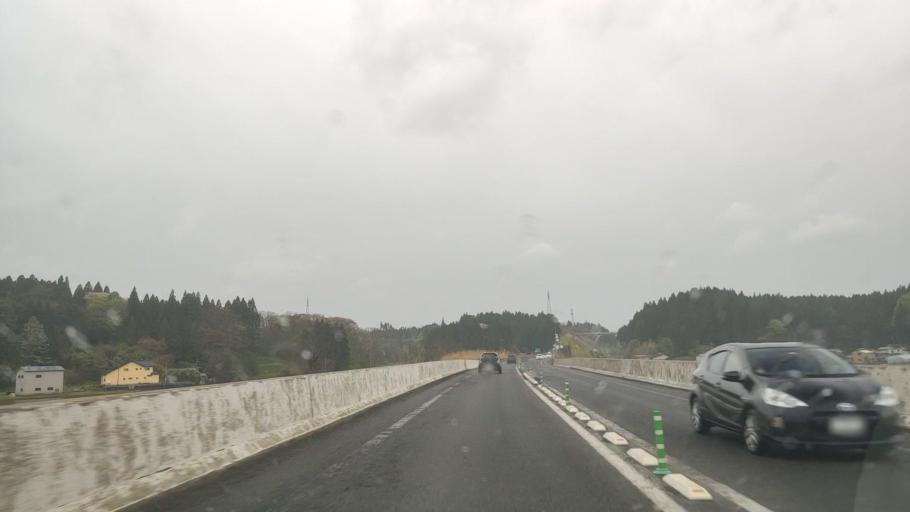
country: JP
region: Akita
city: Noshiromachi
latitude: 40.1858
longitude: 140.0957
